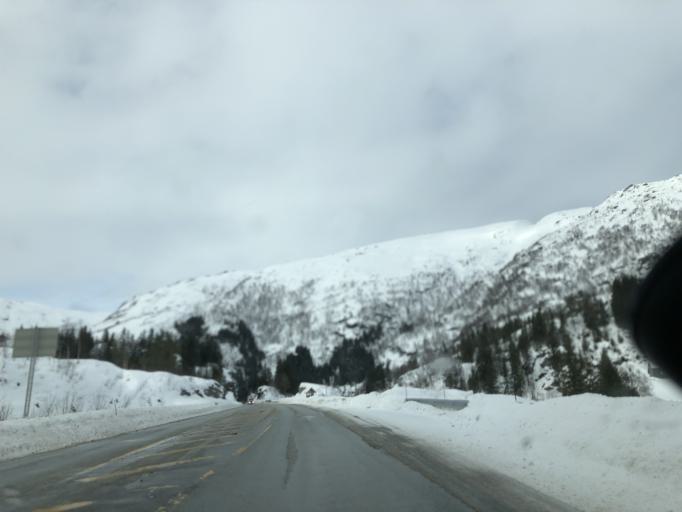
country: NO
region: Hordaland
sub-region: Odda
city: Odda
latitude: 59.9067
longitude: 6.5189
